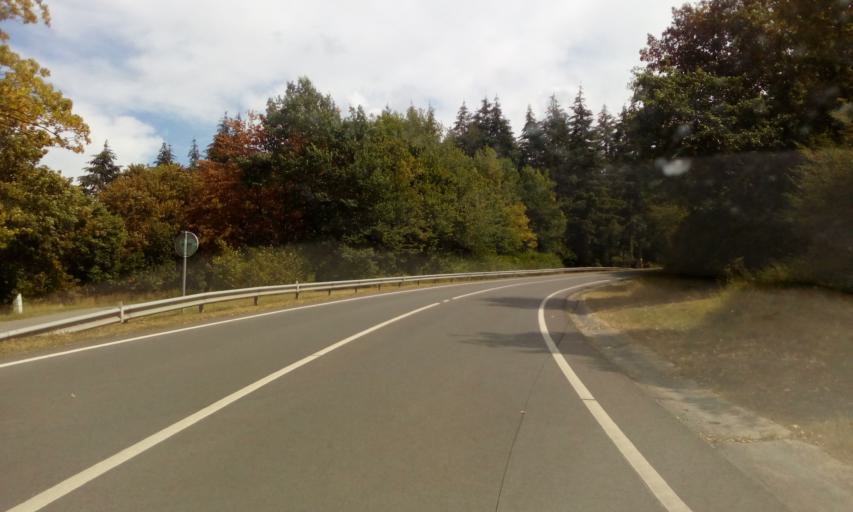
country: BE
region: Wallonia
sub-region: Province du Luxembourg
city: Wellin
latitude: 50.1163
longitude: 5.1165
